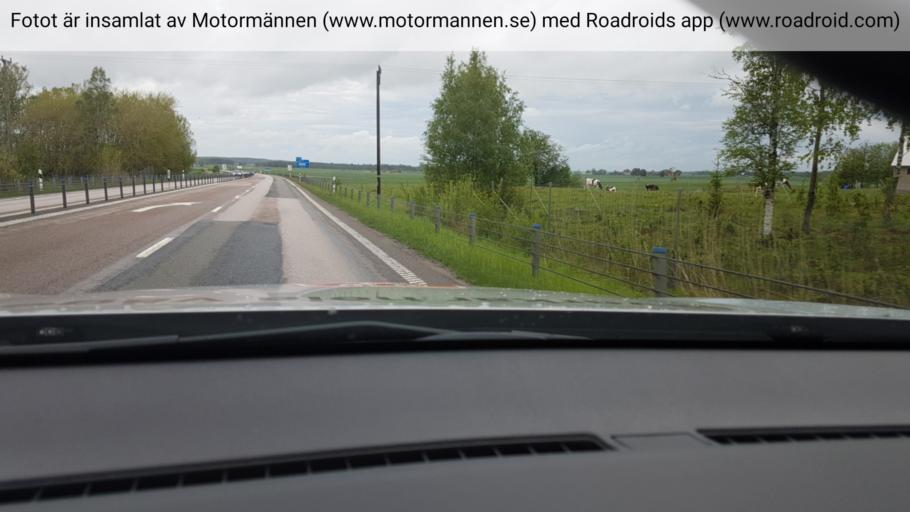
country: SE
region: Vaestra Goetaland
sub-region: Skovde Kommun
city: Stopen
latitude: 58.5460
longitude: 13.8110
